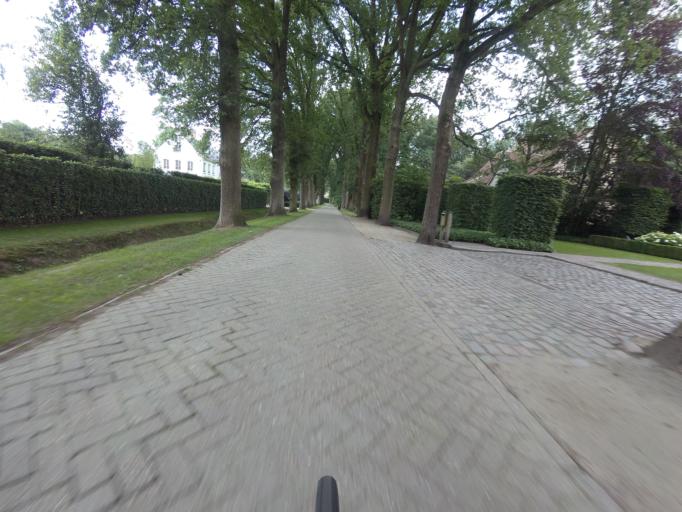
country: BE
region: Flanders
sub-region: Provincie Antwerpen
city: Schilde
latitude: 51.2253
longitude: 4.5631
